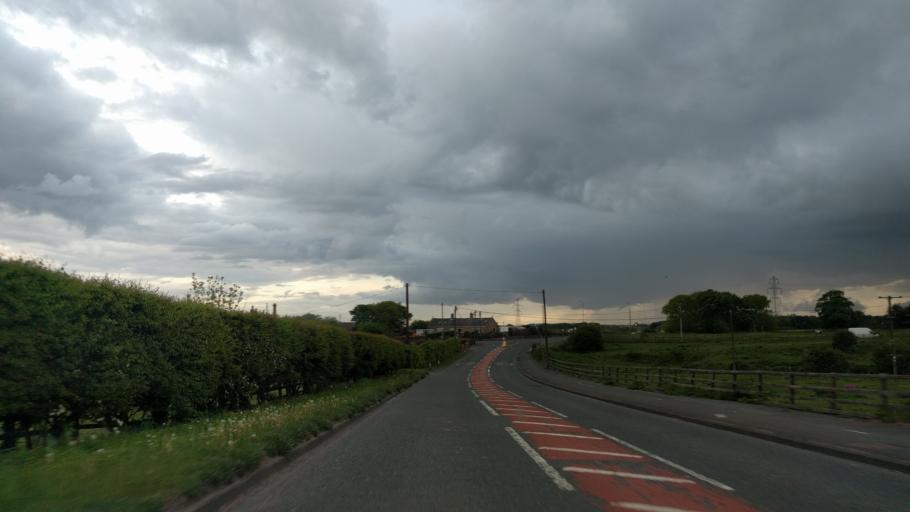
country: GB
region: England
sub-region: Northumberland
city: Newbiggin-by-the-Sea
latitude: 55.1951
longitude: -1.5323
